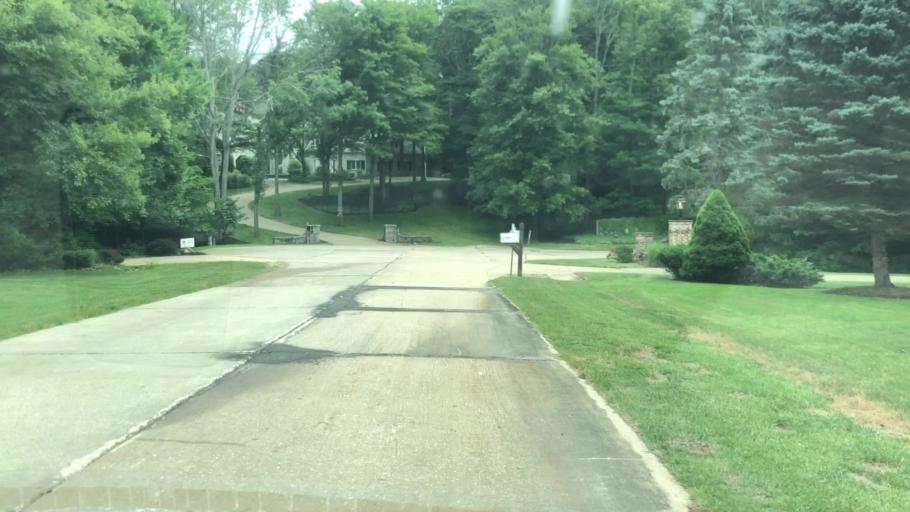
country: US
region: Ohio
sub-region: Summit County
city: Montrose-Ghent
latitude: 41.1598
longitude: -81.6123
